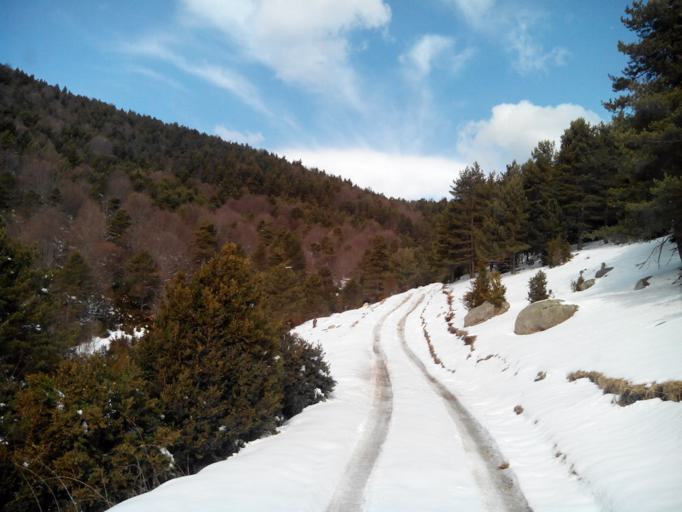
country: ES
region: Catalonia
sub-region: Provincia de Barcelona
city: Sant Julia de Cerdanyola
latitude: 42.1982
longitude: 1.9405
